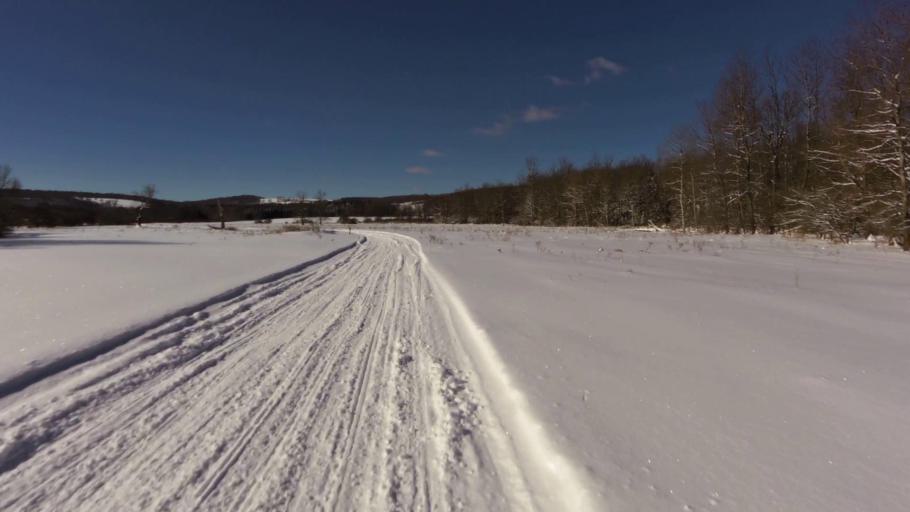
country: US
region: New York
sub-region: Chautauqua County
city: Silver Creek
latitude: 42.3703
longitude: -79.1662
